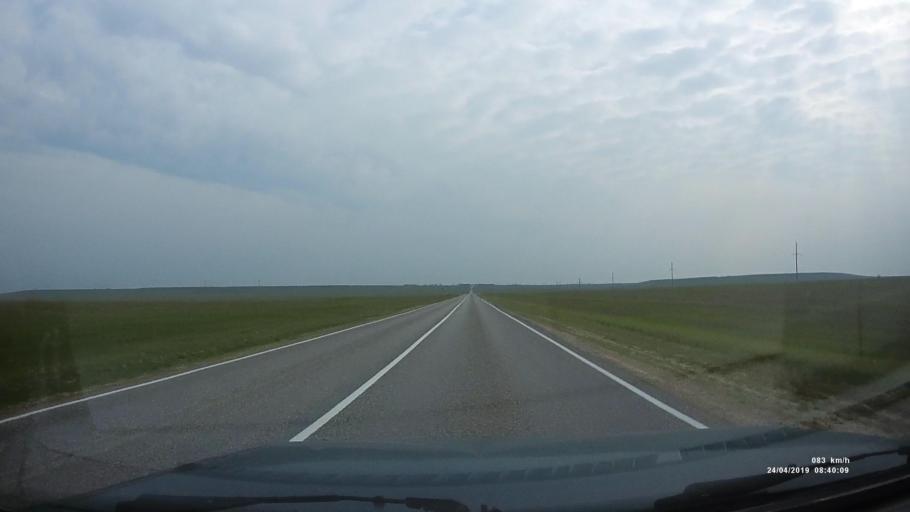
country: RU
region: Kalmykiya
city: Arshan'
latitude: 46.2248
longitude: 43.9960
